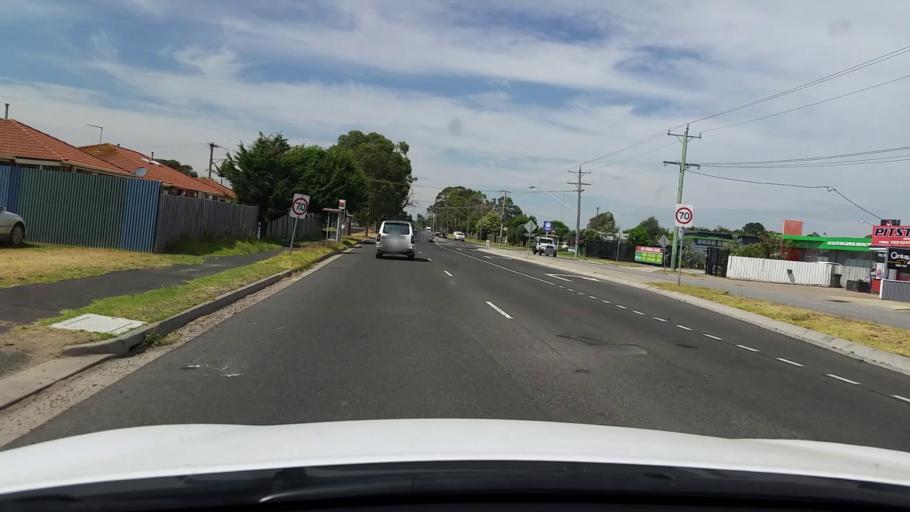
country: AU
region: Victoria
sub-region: Mornington Peninsula
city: Hastings
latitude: -38.3088
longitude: 145.1837
